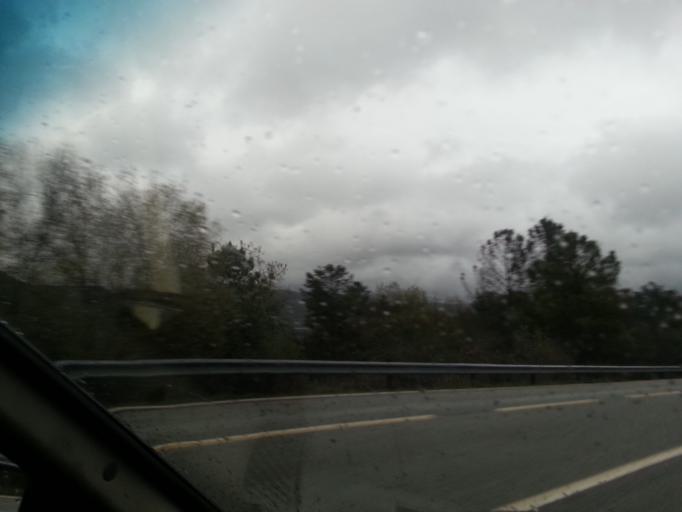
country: PT
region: Guarda
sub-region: Fornos de Algodres
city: Fornos de Algodres
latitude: 40.6161
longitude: -7.6055
